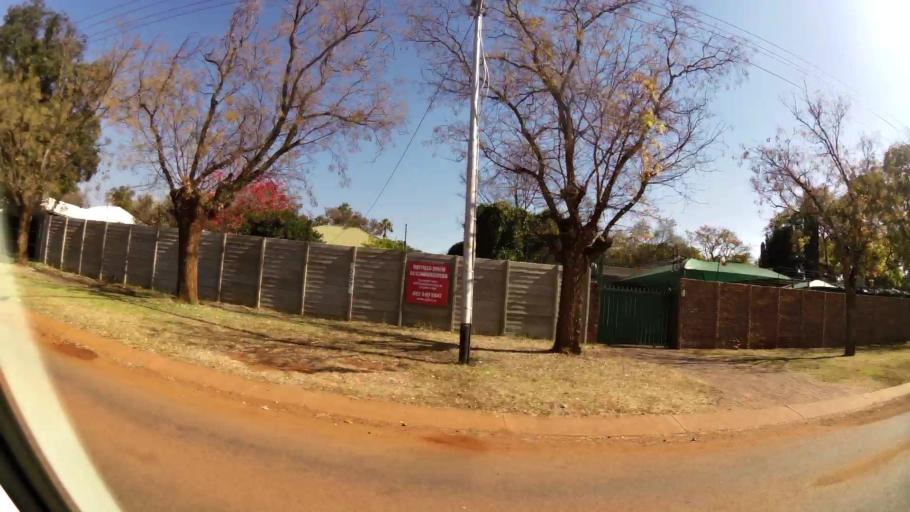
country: ZA
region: Gauteng
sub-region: City of Tshwane Metropolitan Municipality
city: Pretoria
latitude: -25.7473
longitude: 28.2447
